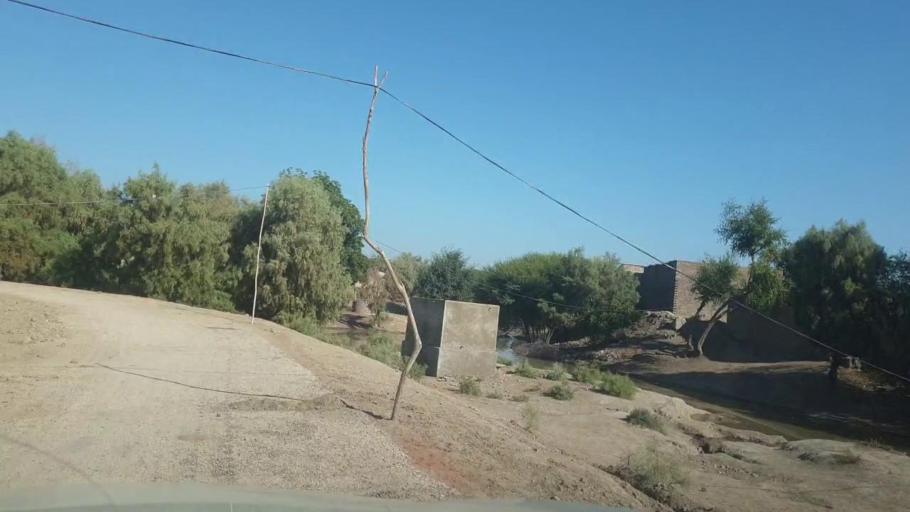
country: PK
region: Sindh
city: Bhan
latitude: 26.5496
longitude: 67.6544
